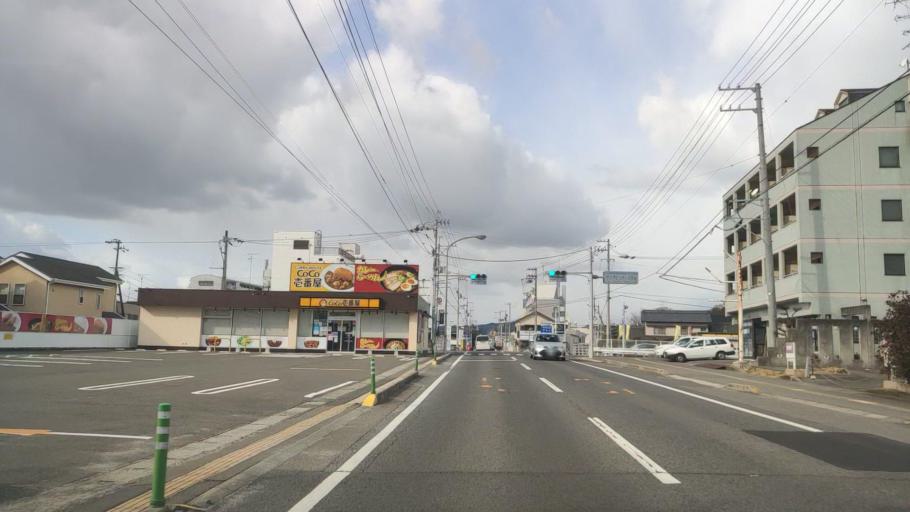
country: JP
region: Ehime
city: Saijo
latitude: 34.0477
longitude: 133.0180
